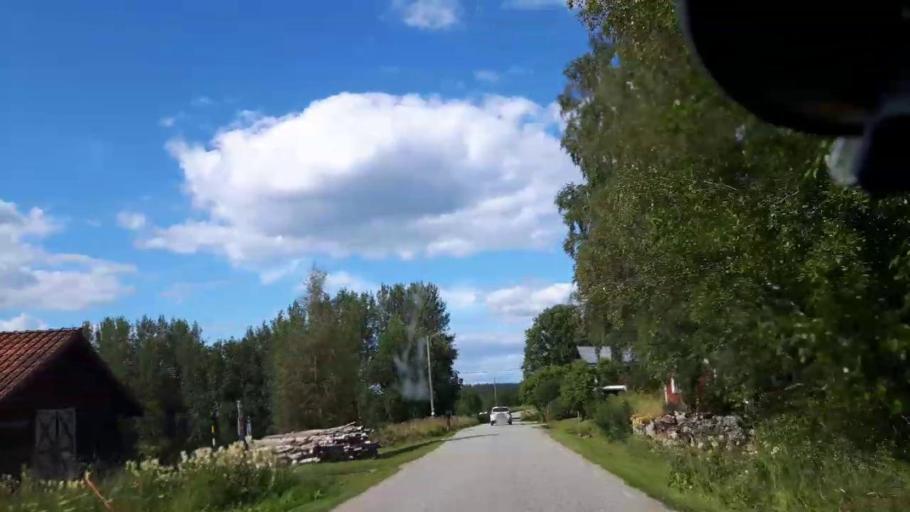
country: SE
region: Jaemtland
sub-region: Braecke Kommun
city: Braecke
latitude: 62.8752
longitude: 15.2729
